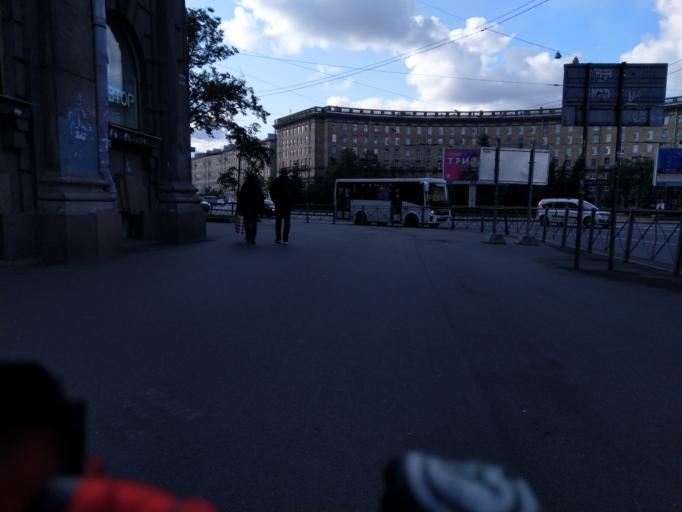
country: RU
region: St.-Petersburg
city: Avtovo
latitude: 59.8771
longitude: 30.2587
